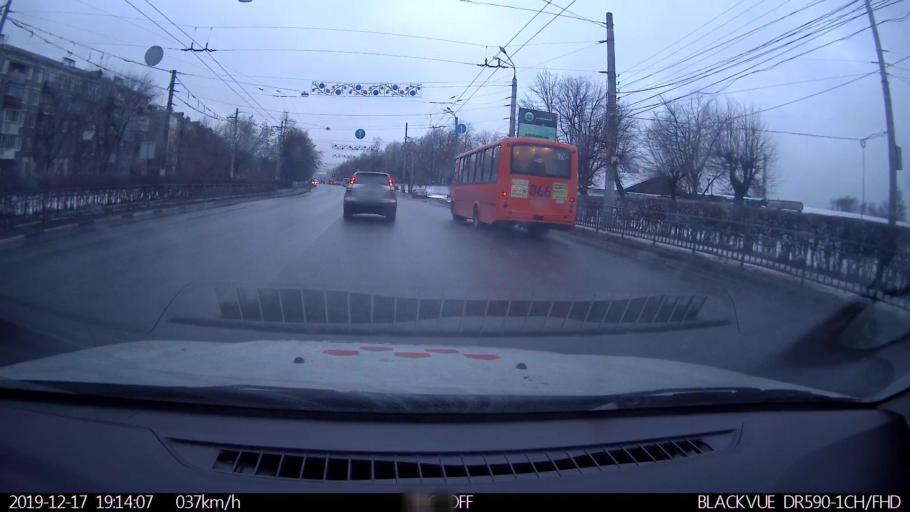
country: RU
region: Nizjnij Novgorod
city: Nizhniy Novgorod
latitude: 56.3247
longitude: 43.9143
